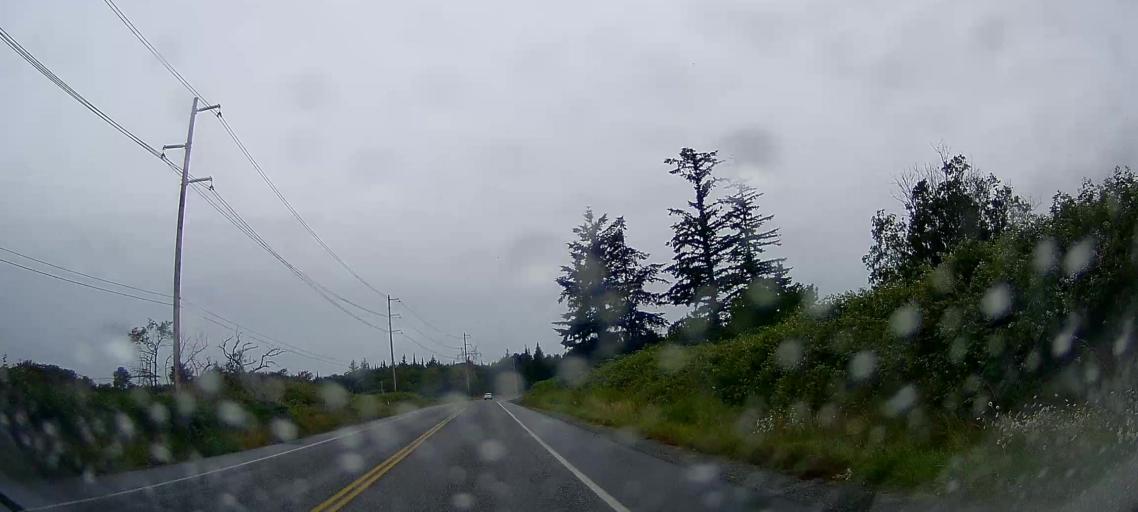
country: US
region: Washington
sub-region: Whatcom County
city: Birch Bay
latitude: 48.8531
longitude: -122.6990
